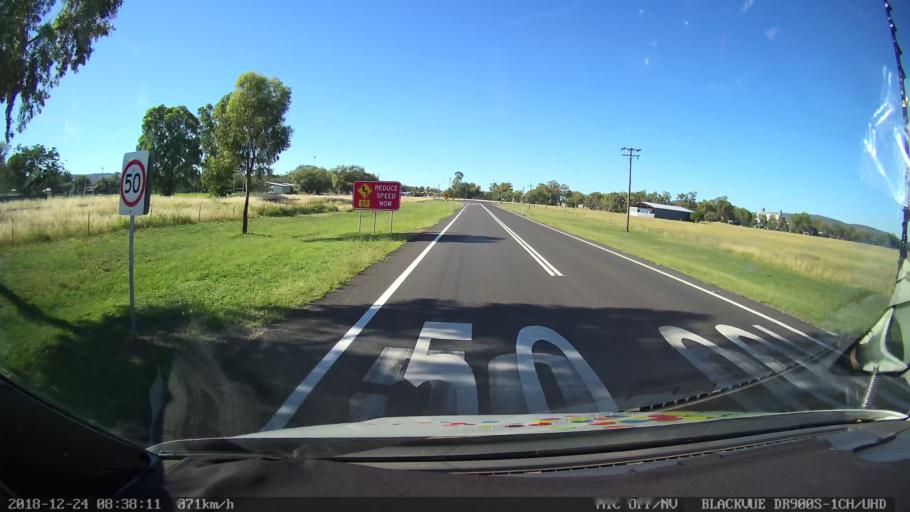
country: AU
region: New South Wales
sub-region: Liverpool Plains
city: Quirindi
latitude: -31.3387
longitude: 150.6476
